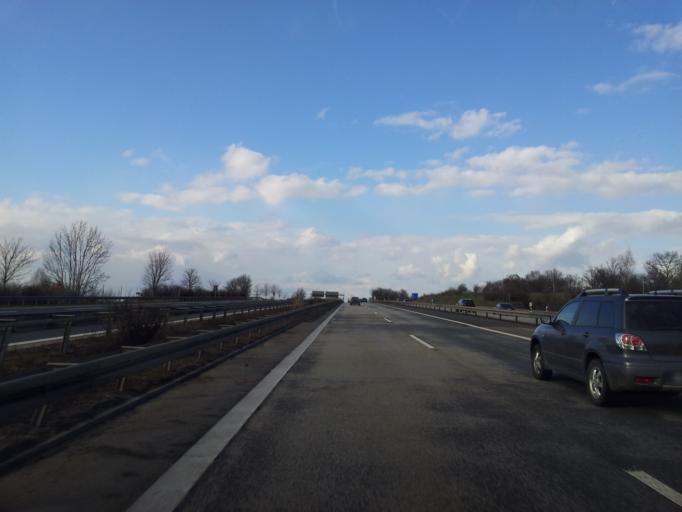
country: DE
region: Saxony
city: Albertstadt
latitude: 51.1245
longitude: 13.7475
